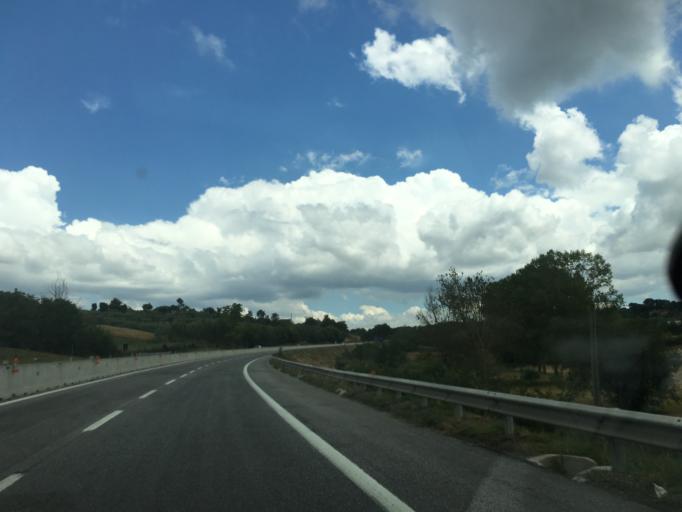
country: IT
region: Campania
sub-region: Provincia di Avellino
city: Passo di Mirabella-Pianopantano
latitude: 41.0596
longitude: 15.0251
